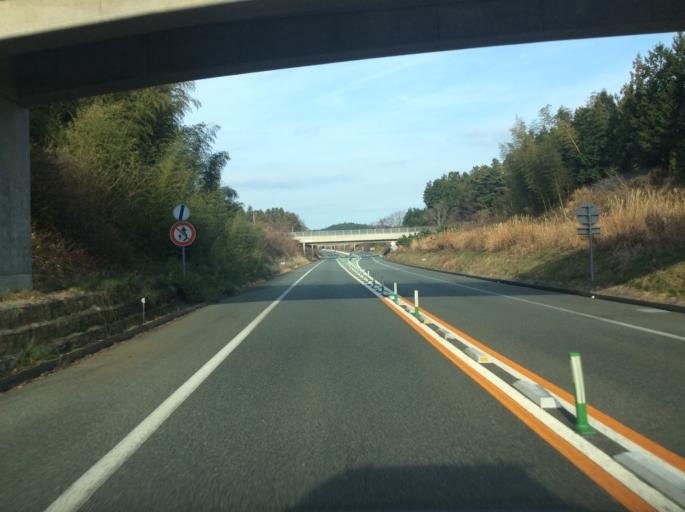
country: JP
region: Fukushima
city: Namie
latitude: 37.2970
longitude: 140.9858
